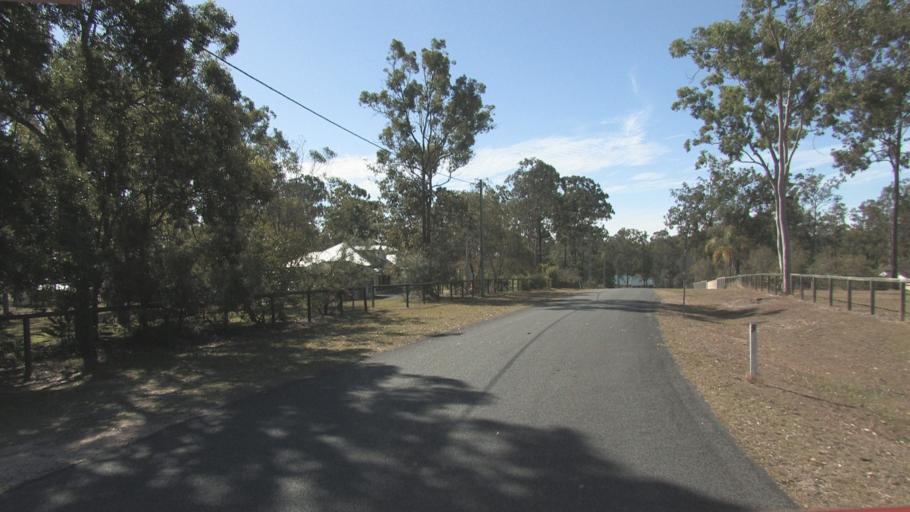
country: AU
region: Queensland
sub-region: Ipswich
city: Springfield Lakes
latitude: -27.7269
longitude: 152.9588
